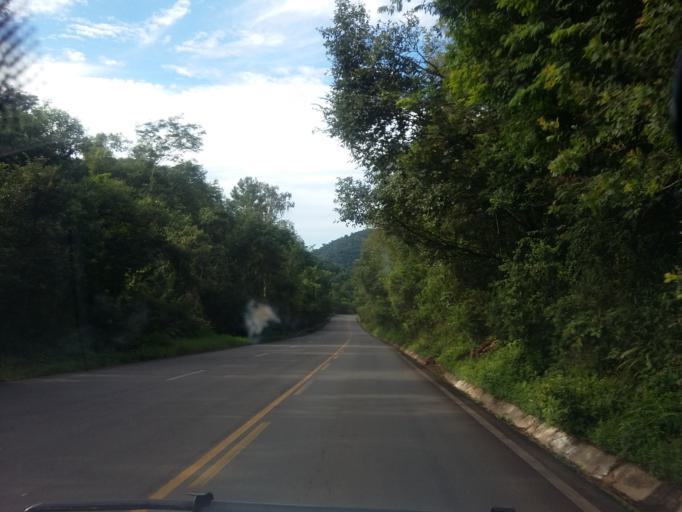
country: BR
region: Santa Catarina
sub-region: Celso Ramos
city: Celso Ramos
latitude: -27.6131
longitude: -51.4747
